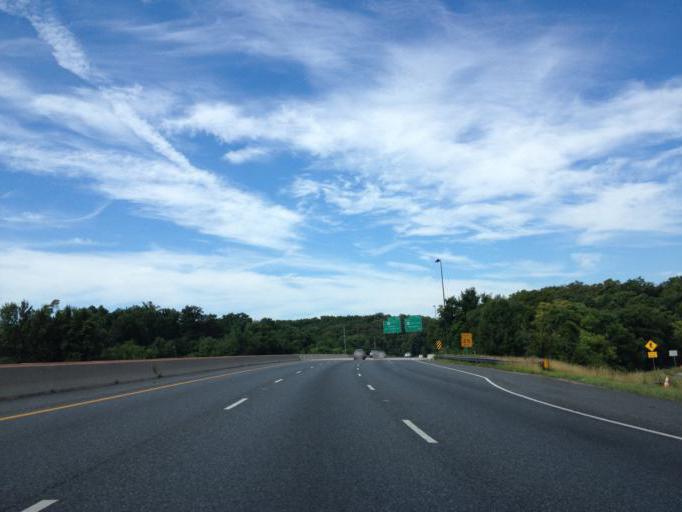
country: US
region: Maryland
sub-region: Anne Arundel County
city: Parole
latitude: 38.9957
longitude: -76.5133
